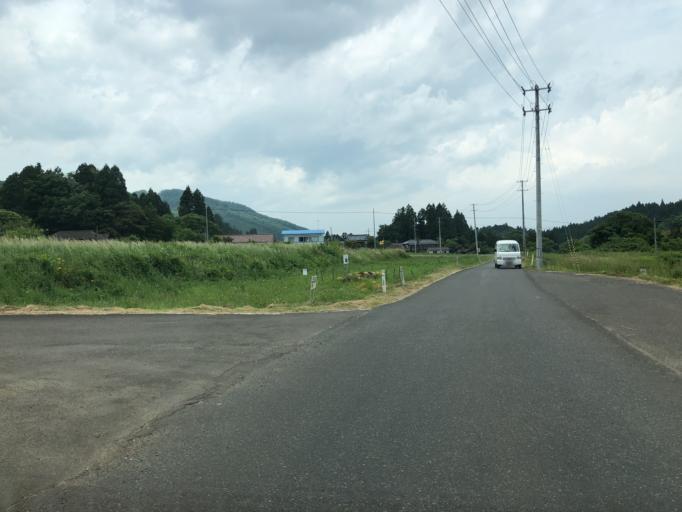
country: JP
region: Miyagi
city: Marumori
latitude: 37.8315
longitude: 140.8360
